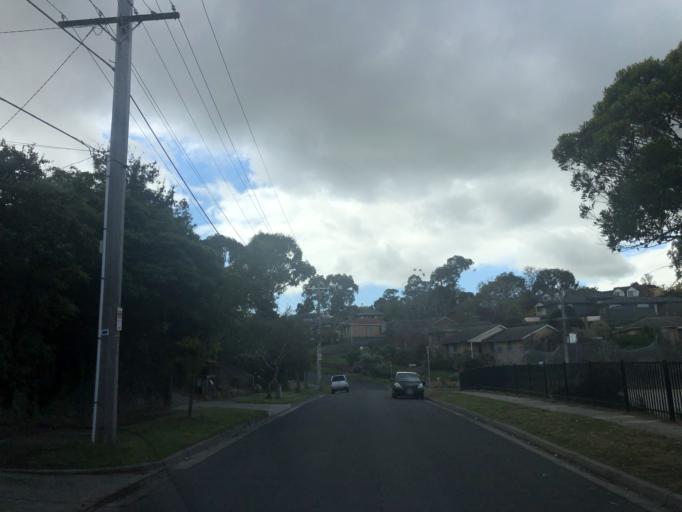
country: AU
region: Victoria
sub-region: Whitehorse
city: Burwood
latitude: -37.8671
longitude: 145.1335
